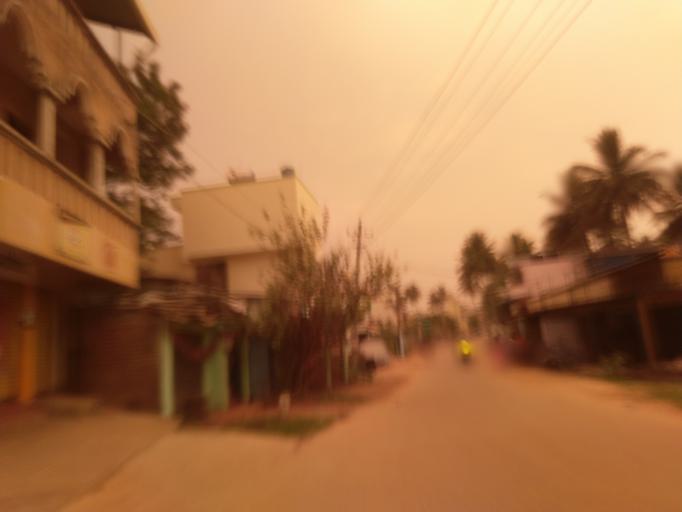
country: IN
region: Karnataka
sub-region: Hassan
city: Hassan
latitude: 13.0142
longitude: 76.1097
